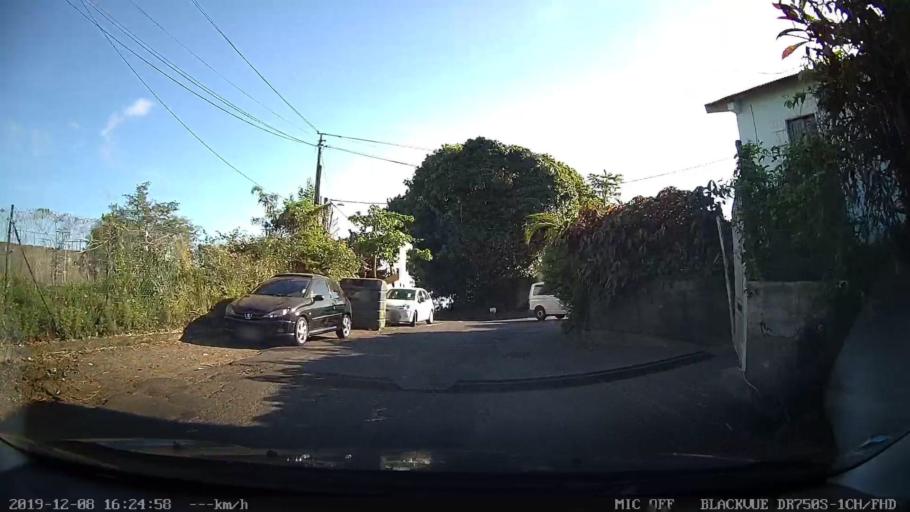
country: RE
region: Reunion
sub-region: Reunion
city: Sainte-Marie
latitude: -20.9277
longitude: 55.5311
